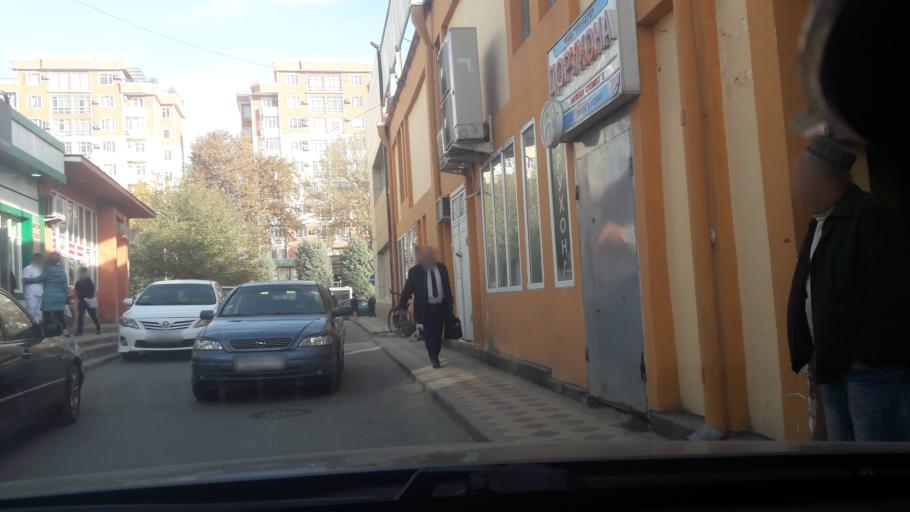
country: TJ
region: Dushanbe
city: Dushanbe
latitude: 38.5835
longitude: 68.7599
